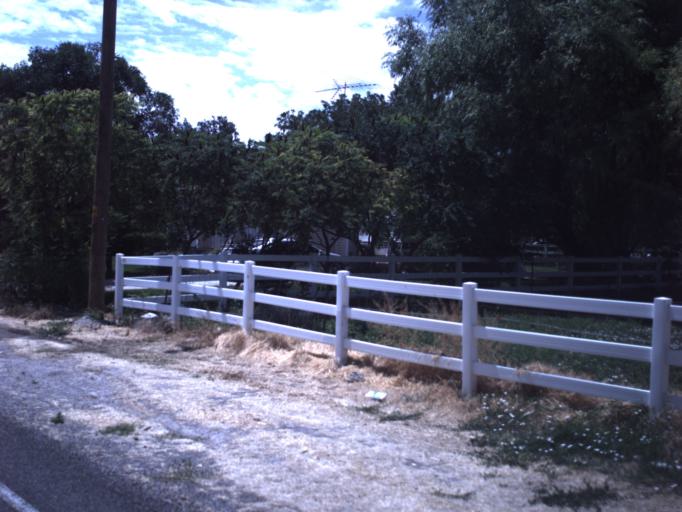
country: US
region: Utah
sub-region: Box Elder County
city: Tremonton
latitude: 41.6807
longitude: -112.2969
